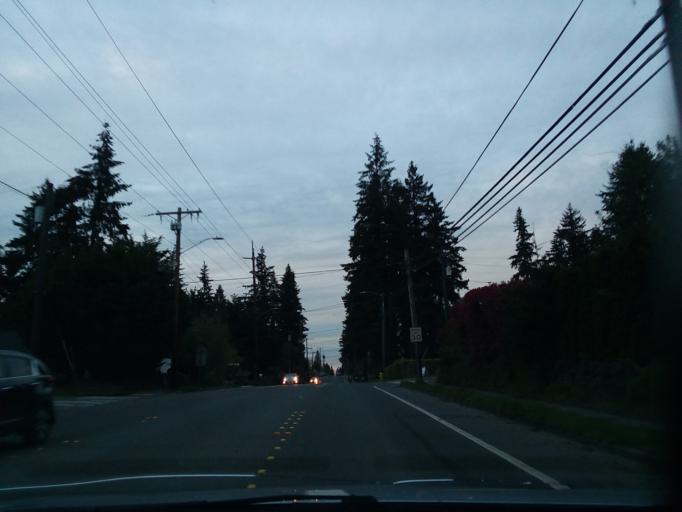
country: US
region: Washington
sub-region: Snohomish County
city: Lynnwood
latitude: 47.8156
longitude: -122.3358
